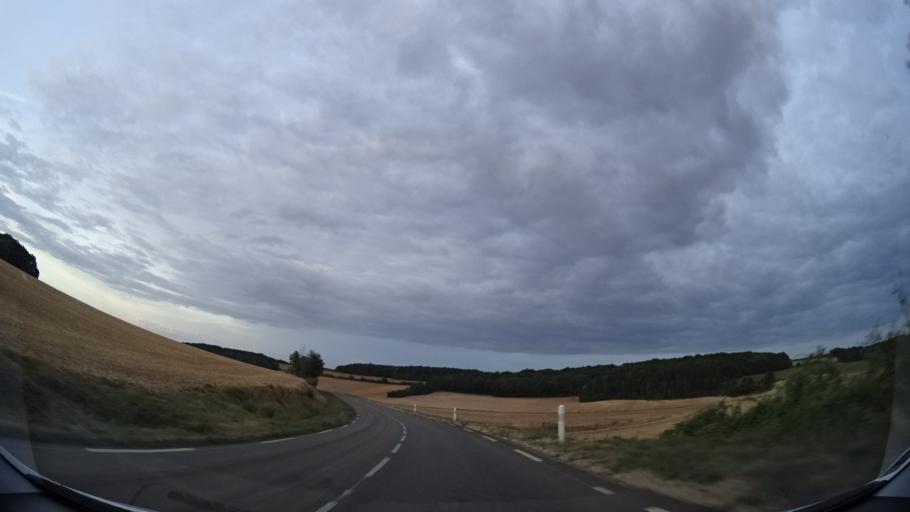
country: FR
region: Bourgogne
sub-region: Departement de l'Yonne
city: Saint-Julien-du-Sault
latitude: 47.9313
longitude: 3.2187
